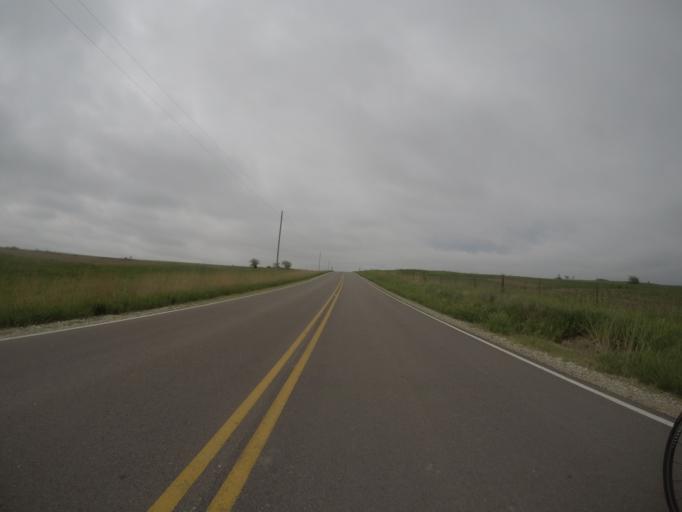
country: US
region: Kansas
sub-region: Pottawatomie County
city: Westmoreland
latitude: 39.5079
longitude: -96.2012
